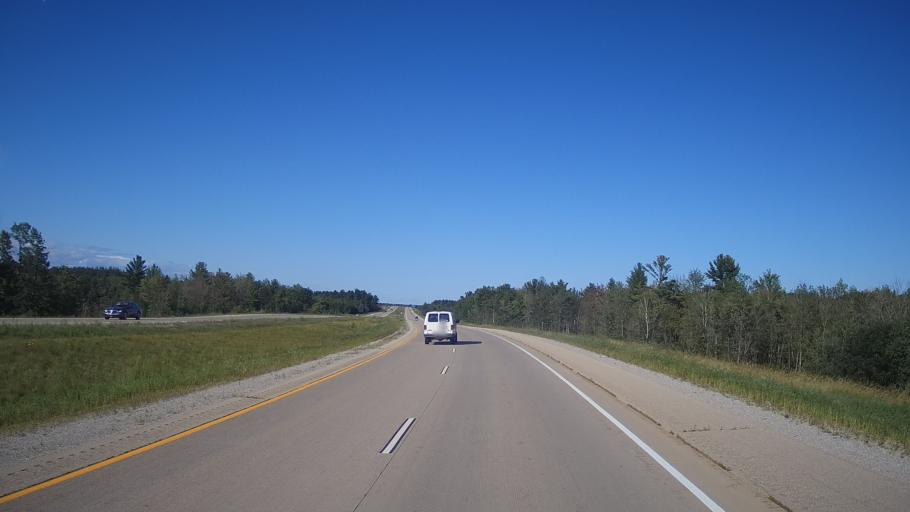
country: US
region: Wisconsin
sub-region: Marinette County
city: Peshtigo
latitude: 45.0418
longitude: -87.7339
